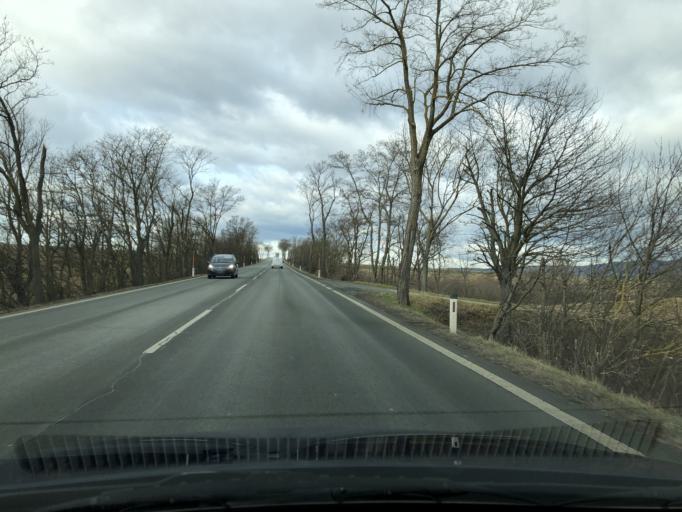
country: AT
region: Burgenland
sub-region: Politischer Bezirk Oberwart
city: Schachendorf
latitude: 47.2586
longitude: 16.4609
